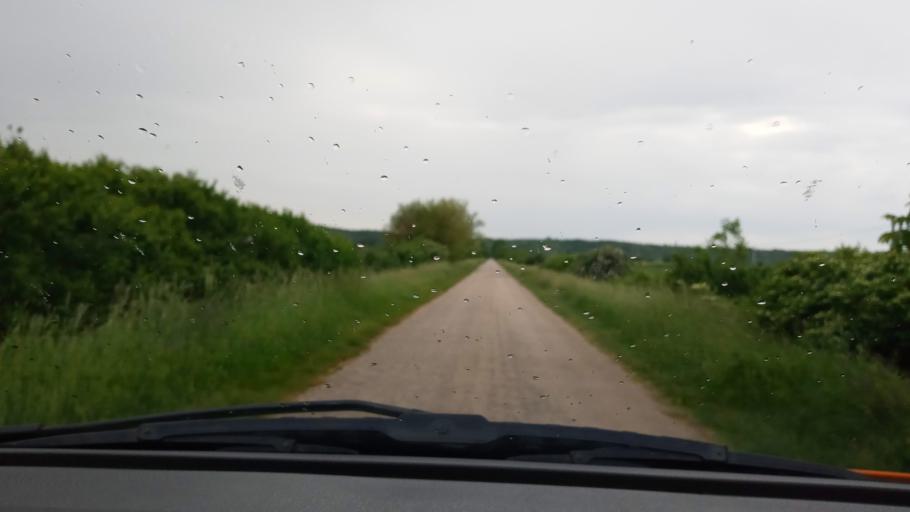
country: HU
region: Baranya
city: Harkany
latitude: 45.9090
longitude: 18.1394
